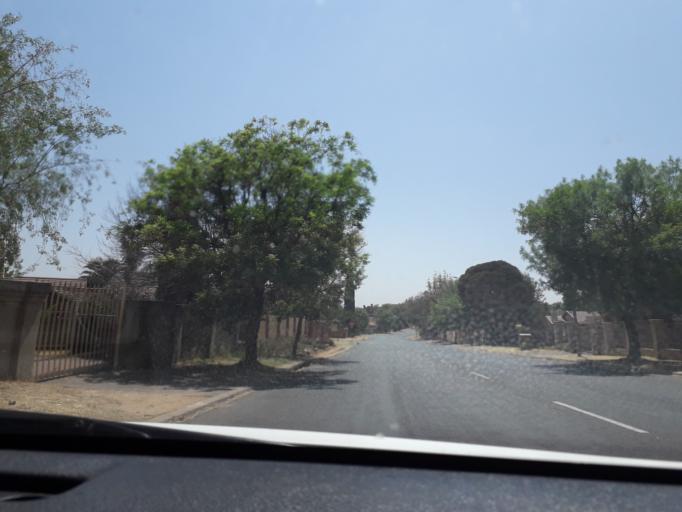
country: ZA
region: Gauteng
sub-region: Ekurhuleni Metropolitan Municipality
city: Tembisa
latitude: -26.0564
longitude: 28.2216
